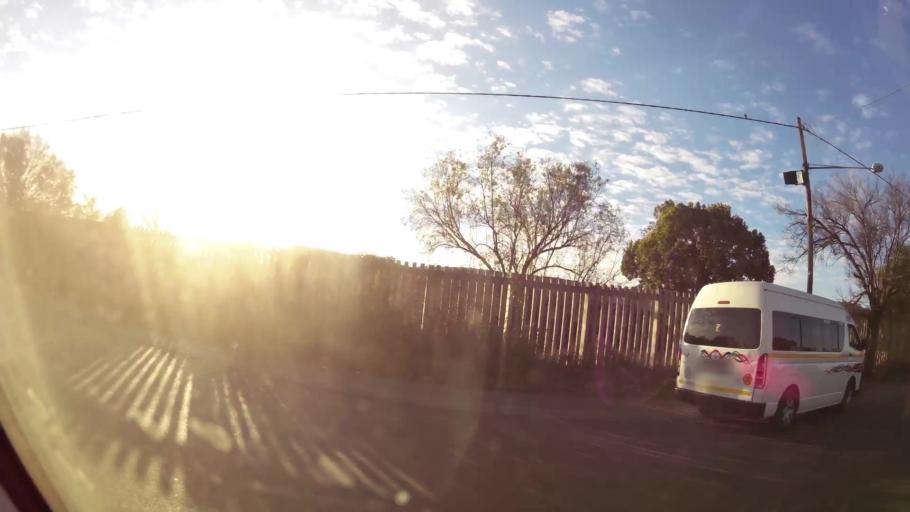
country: ZA
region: Gauteng
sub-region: City of Tshwane Metropolitan Municipality
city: Cullinan
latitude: -25.7099
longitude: 28.3710
